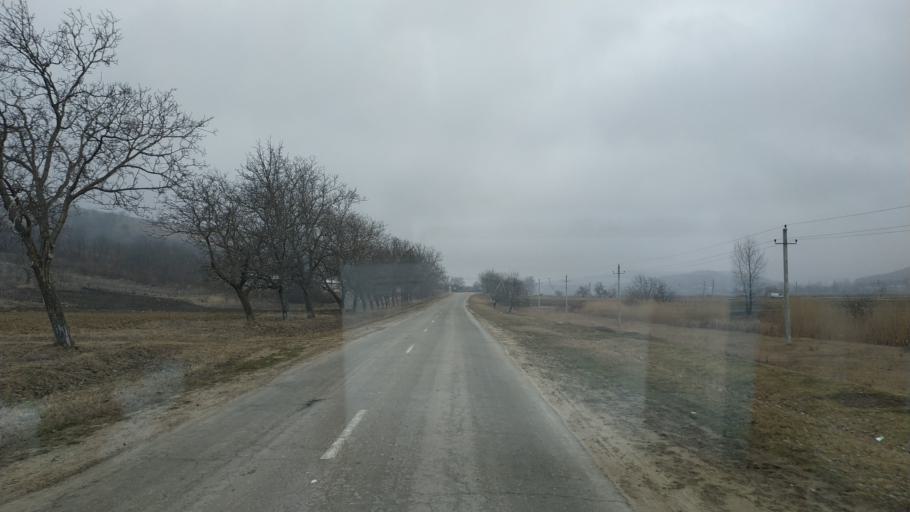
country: MD
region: Hincesti
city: Hincesti
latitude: 46.9660
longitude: 28.4801
